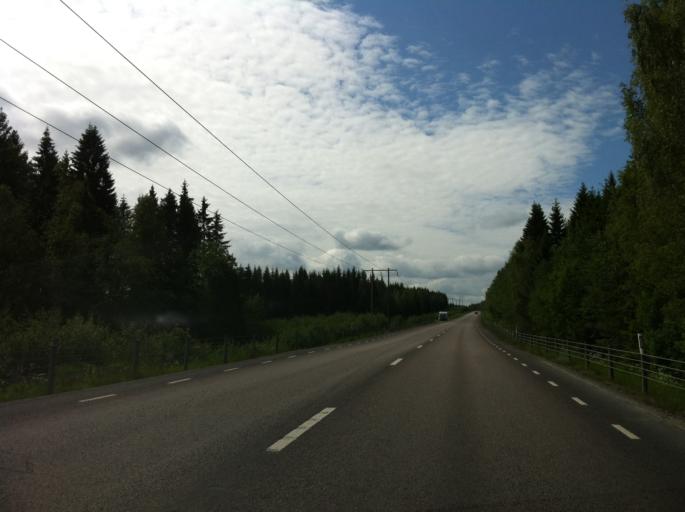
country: SE
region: Vaermland
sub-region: Karlstads Kommun
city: Edsvalla
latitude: 59.4273
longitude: 13.1963
